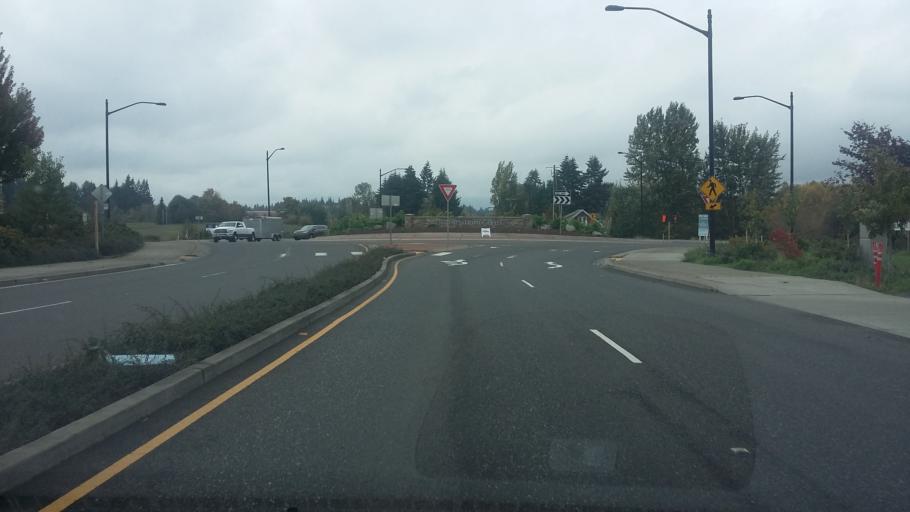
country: US
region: Washington
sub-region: Clark County
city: La Center
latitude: 45.8159
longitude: -122.6896
